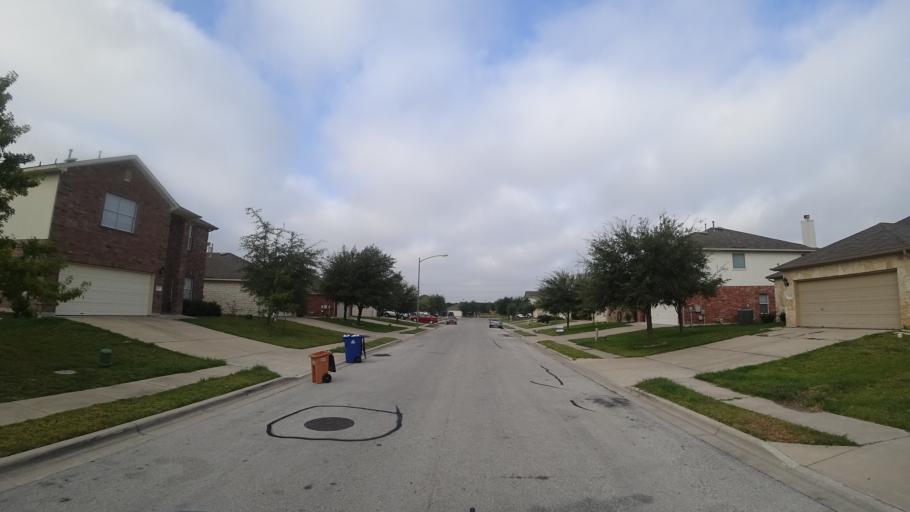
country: US
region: Texas
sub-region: Travis County
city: Pflugerville
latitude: 30.3605
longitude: -97.6436
